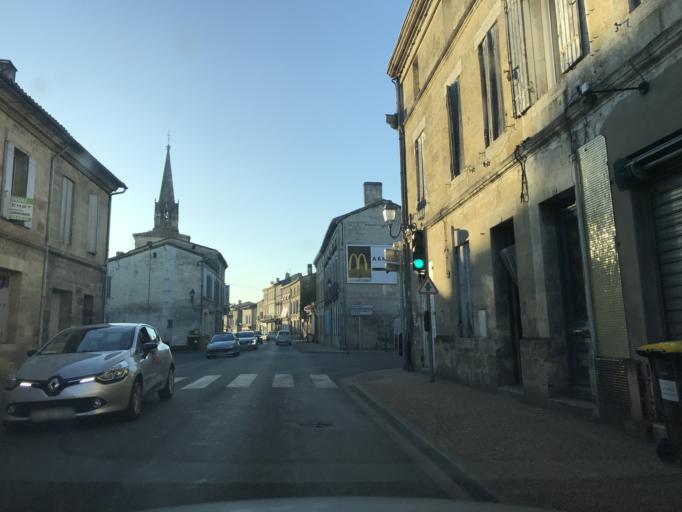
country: FR
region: Aquitaine
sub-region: Departement de la Gironde
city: Saint-Medard-de-Guizieres
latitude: 45.0155
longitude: -0.0575
